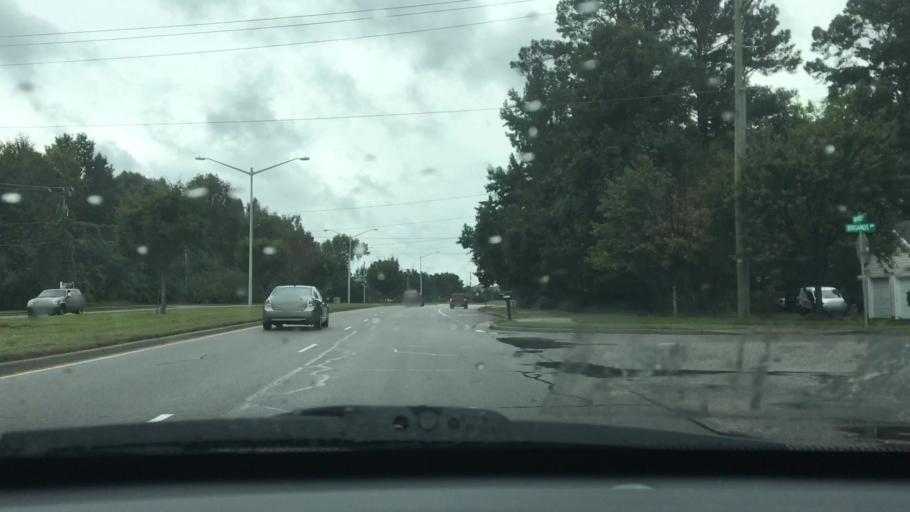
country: US
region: Virginia
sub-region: City of Virginia Beach
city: Virginia Beach
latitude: 36.7805
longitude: -76.0841
